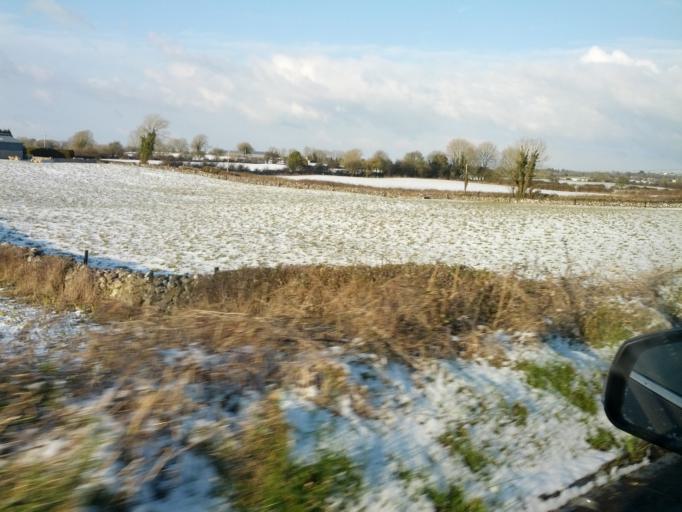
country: IE
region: Connaught
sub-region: County Galway
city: Athenry
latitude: 53.1849
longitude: -8.7238
